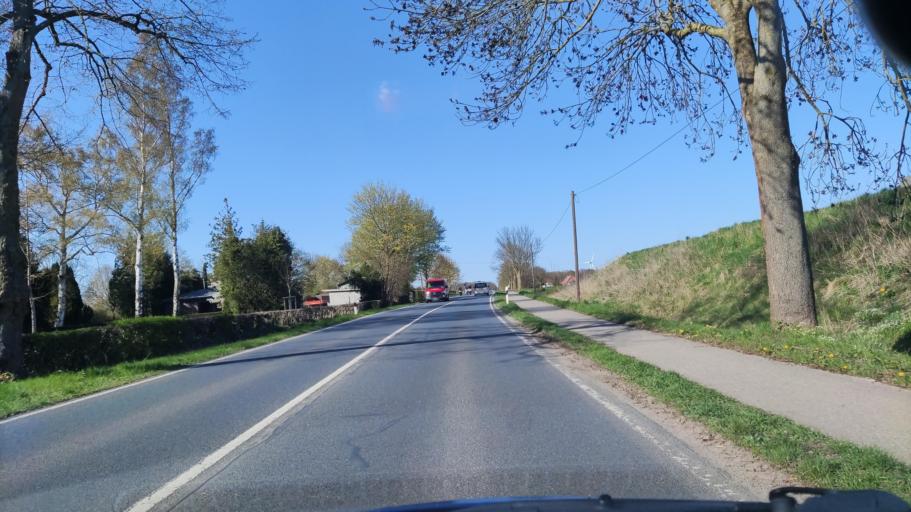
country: DE
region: Lower Saxony
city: Sehnde
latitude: 52.3251
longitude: 9.9676
